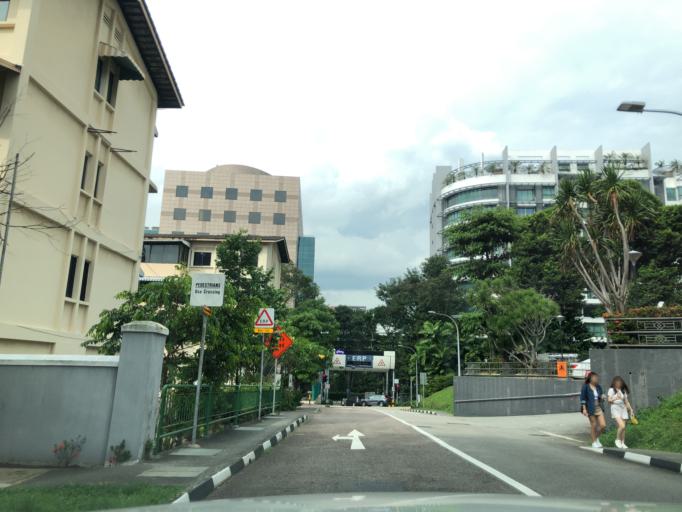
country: SG
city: Singapore
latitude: 1.2984
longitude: 103.8411
